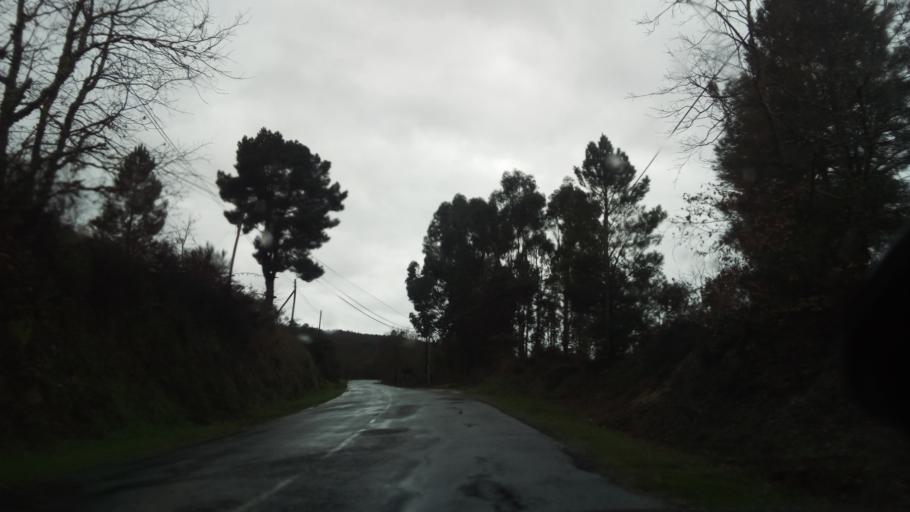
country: PT
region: Guarda
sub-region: Celorico da Beira
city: Celorico da Beira
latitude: 40.6295
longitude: -7.4461
